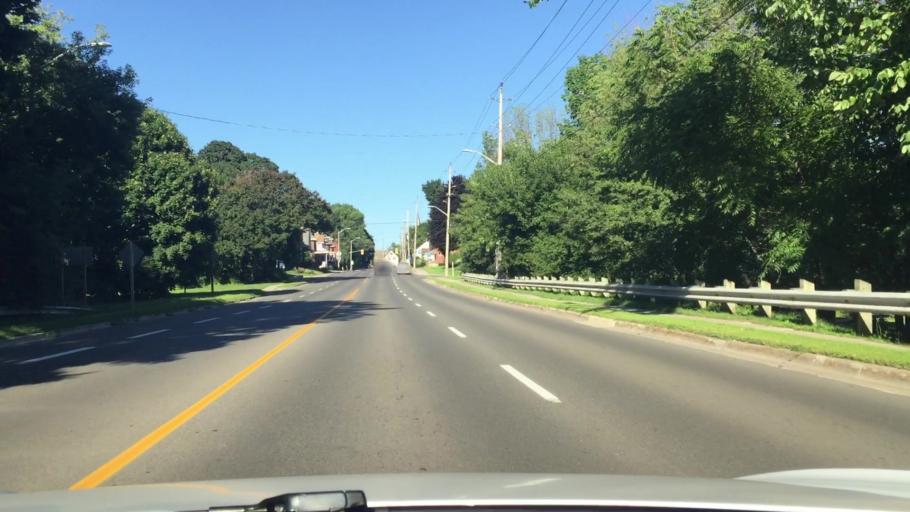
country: CA
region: Ontario
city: Oshawa
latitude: 43.9020
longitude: -78.8728
